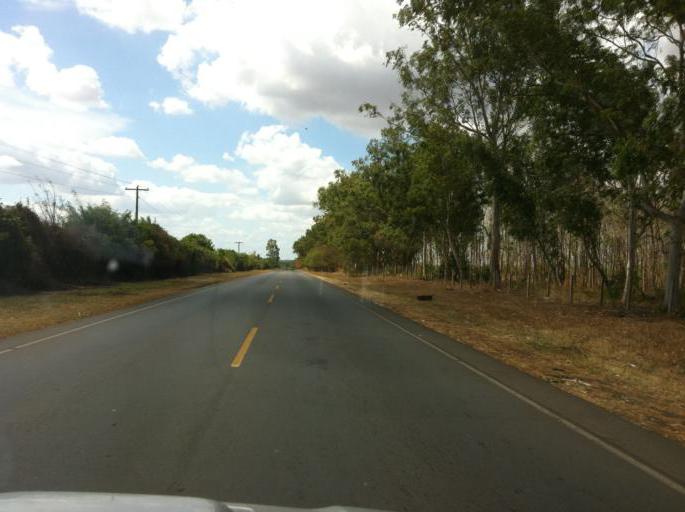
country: NI
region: Masaya
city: Nindiri
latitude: 12.0067
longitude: -86.1040
